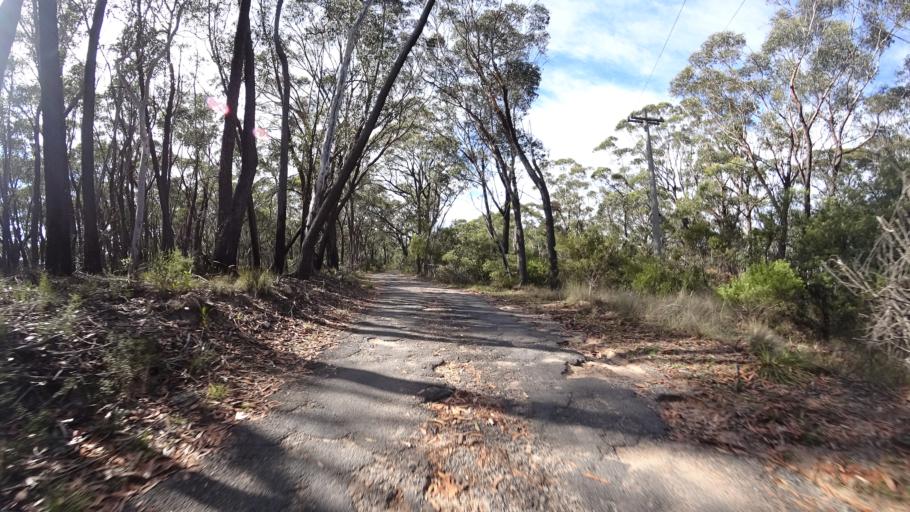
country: AU
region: New South Wales
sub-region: Lithgow
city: Lithgow
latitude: -33.4917
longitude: 150.1642
